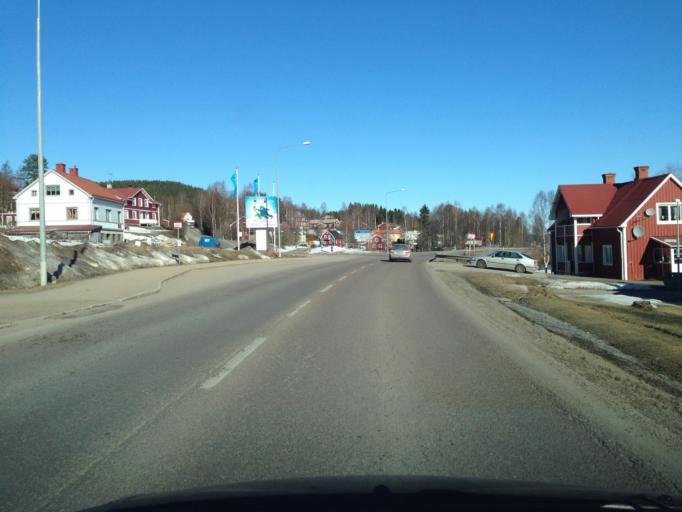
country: SE
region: Gaevleborg
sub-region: Ljusdals Kommun
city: Jaervsoe
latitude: 61.7211
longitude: 16.1683
